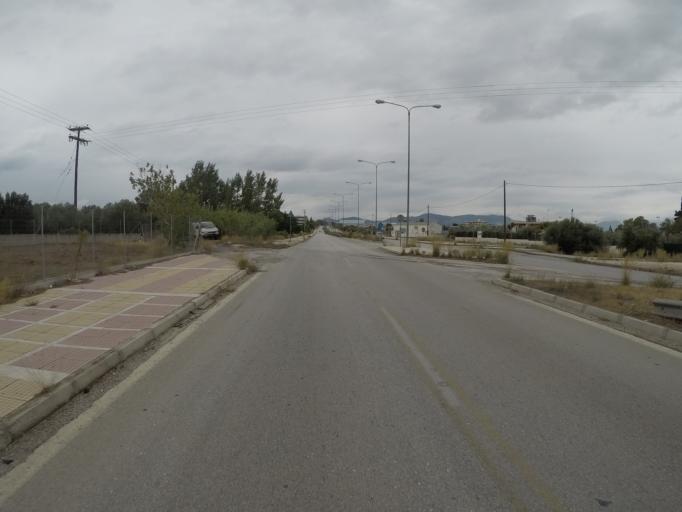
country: GR
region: Peloponnese
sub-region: Nomos Korinthias
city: Loutraki
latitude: 37.9514
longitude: 22.9795
